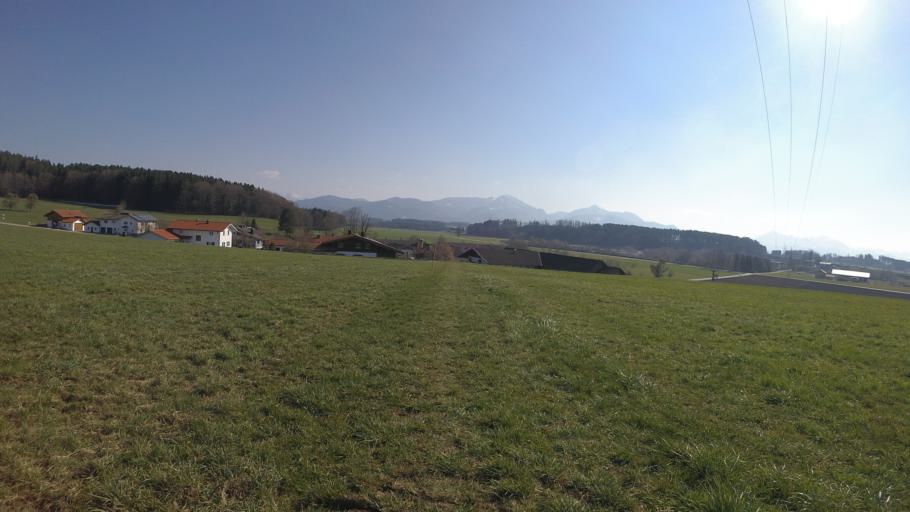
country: DE
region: Bavaria
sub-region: Upper Bavaria
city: Vachendorf
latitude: 47.8656
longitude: 12.5913
